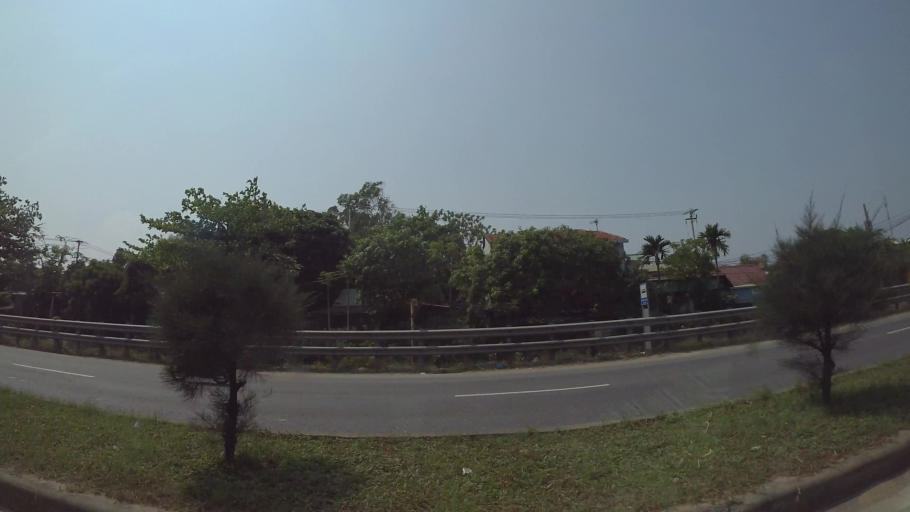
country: VN
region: Da Nang
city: Cam Le
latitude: 16.0046
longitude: 108.1910
